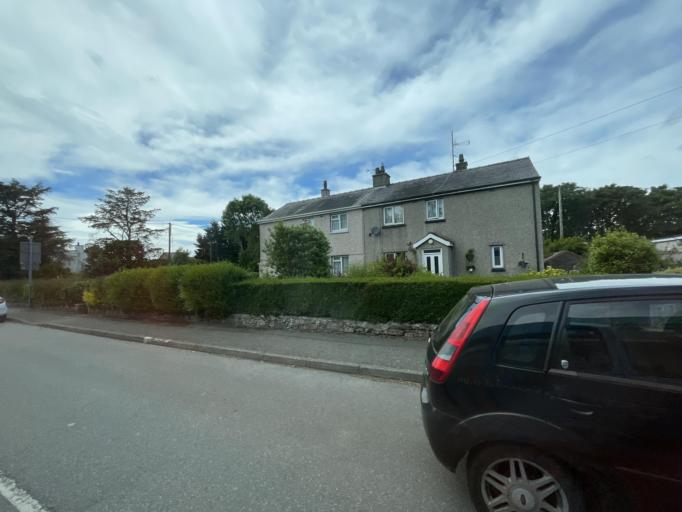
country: GB
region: Wales
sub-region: Anglesey
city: Gaerwen
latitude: 53.2110
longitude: -4.2539
